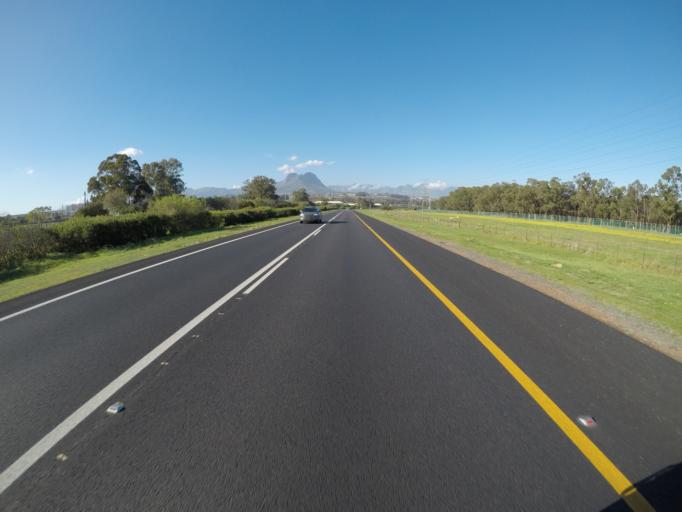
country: ZA
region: Western Cape
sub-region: Cape Winelands District Municipality
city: Stellenbosch
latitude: -34.0589
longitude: 18.7869
